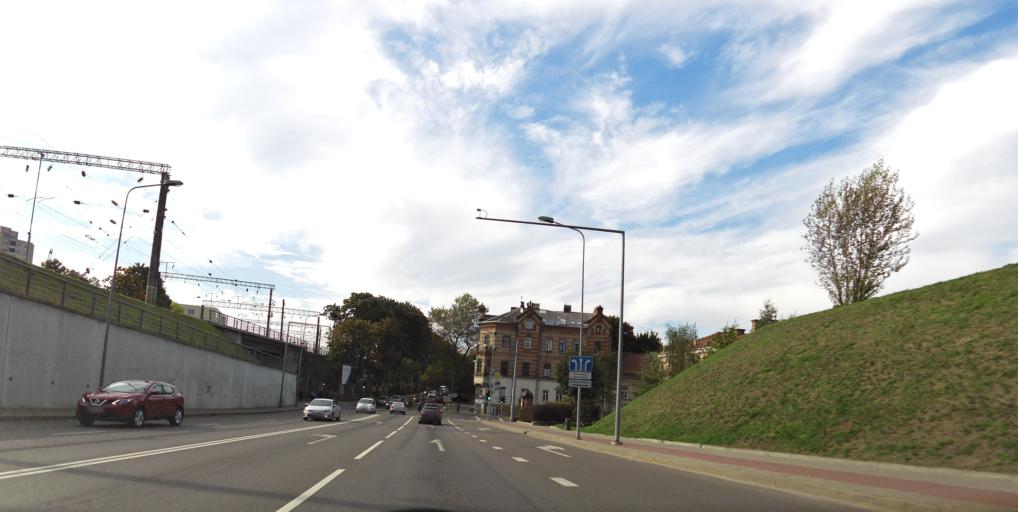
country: LT
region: Vilnius County
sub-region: Vilnius
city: Vilnius
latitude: 54.6725
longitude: 25.2914
